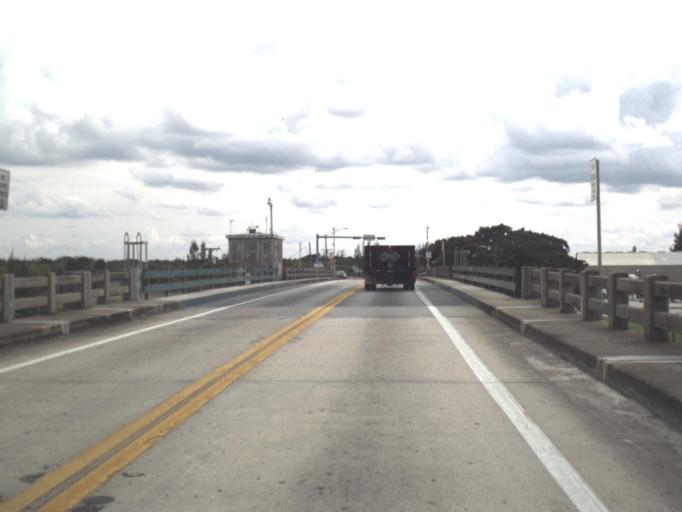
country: US
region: Florida
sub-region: Lee County
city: Fort Myers Shores
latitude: 26.7167
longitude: -81.7608
